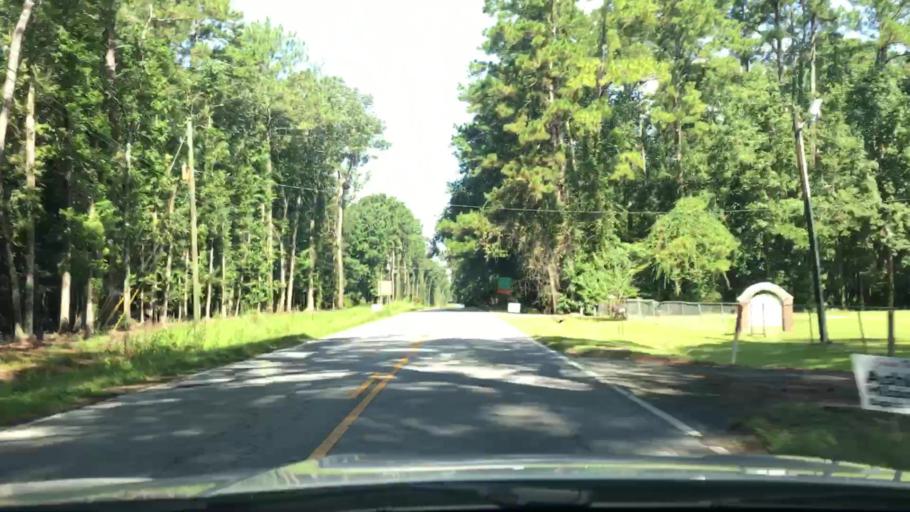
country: US
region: South Carolina
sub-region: Dorchester County
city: Centerville
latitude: 32.9335
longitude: -80.1761
